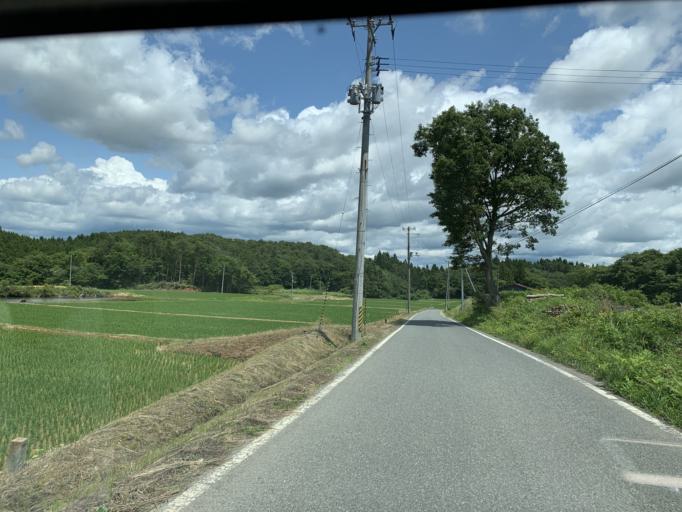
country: JP
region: Iwate
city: Ichinoseki
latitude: 38.9286
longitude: 141.0705
